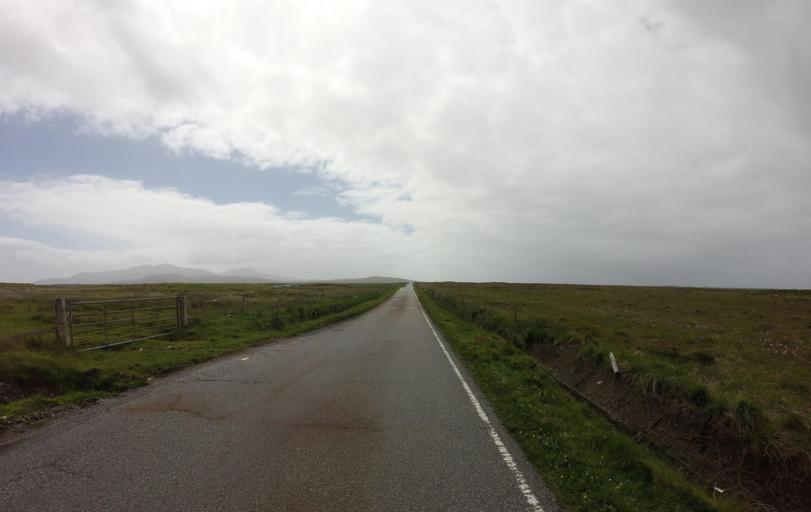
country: GB
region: Scotland
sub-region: Eilean Siar
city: Benbecula
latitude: 57.3795
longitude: -7.3430
